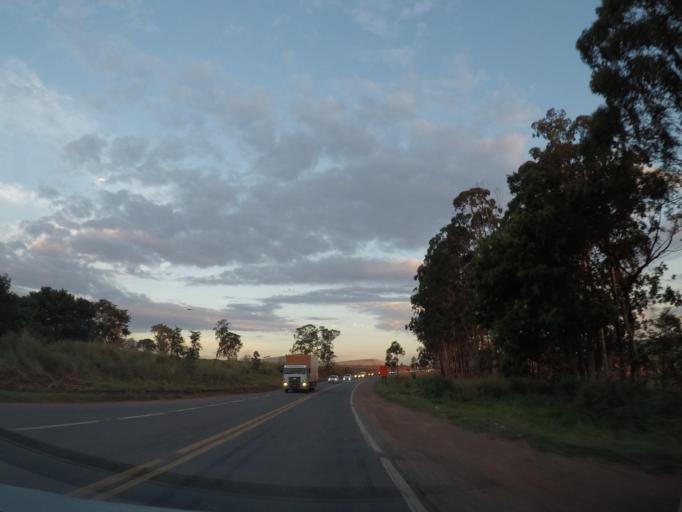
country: BR
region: Sao Paulo
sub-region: Itupeva
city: Itupeva
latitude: -23.0441
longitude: -47.1025
